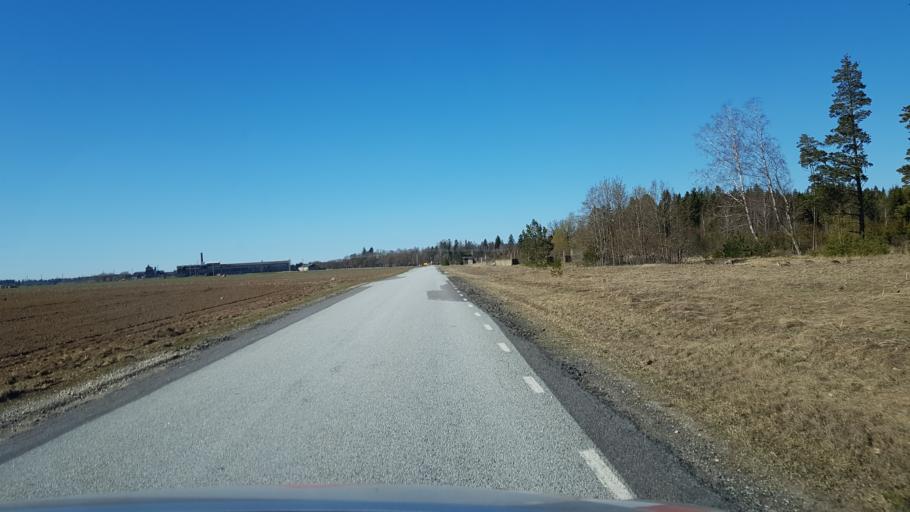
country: EE
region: Laeaene-Virumaa
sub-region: Viru-Nigula vald
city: Kunda
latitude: 59.3848
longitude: 26.5734
